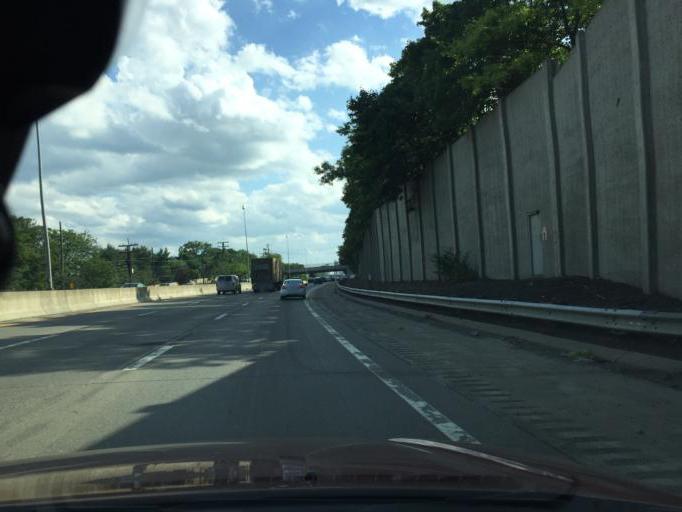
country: US
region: New York
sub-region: Westchester County
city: Larchmont
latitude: 40.9418
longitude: -73.7512
